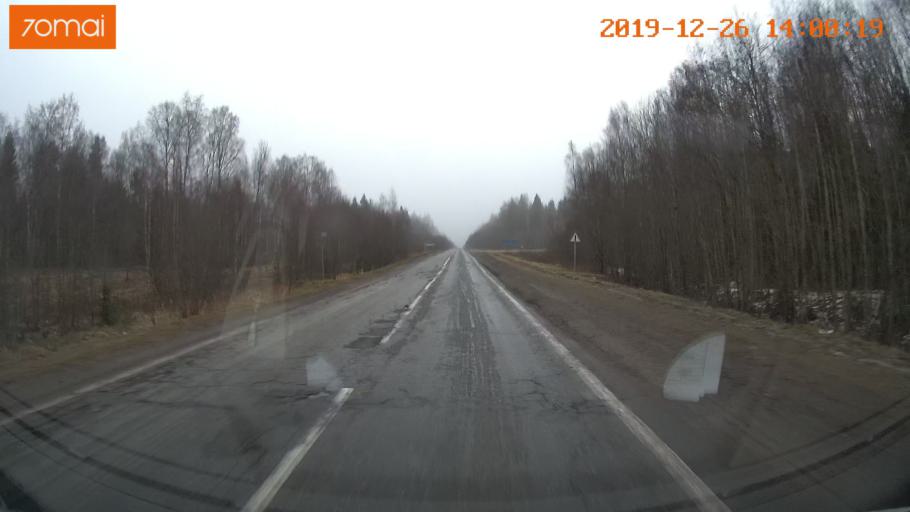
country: RU
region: Jaroslavl
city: Poshekhon'ye
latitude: 58.5590
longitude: 38.7411
